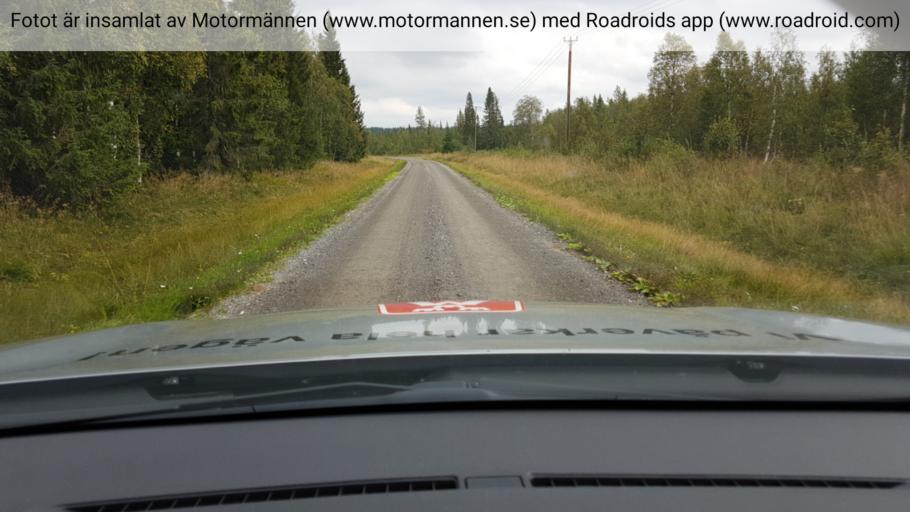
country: SE
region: Jaemtland
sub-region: Stroemsunds Kommun
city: Stroemsund
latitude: 63.7831
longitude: 15.2665
